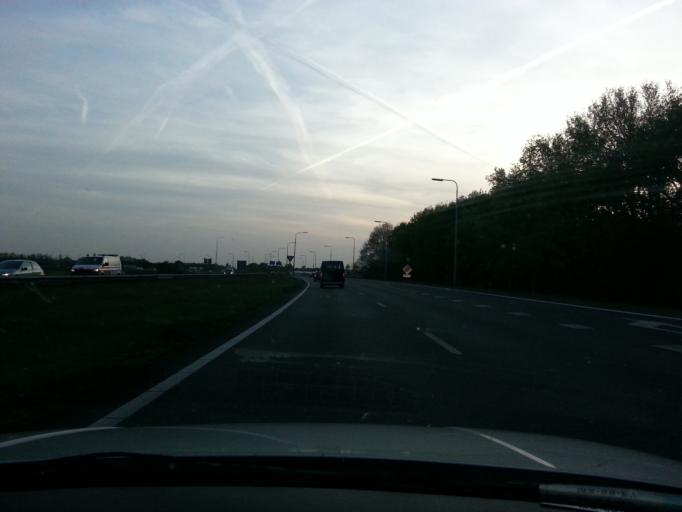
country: NL
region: Friesland
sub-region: Gemeente Skarsterlan
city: Joure
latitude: 52.9590
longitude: 5.8255
